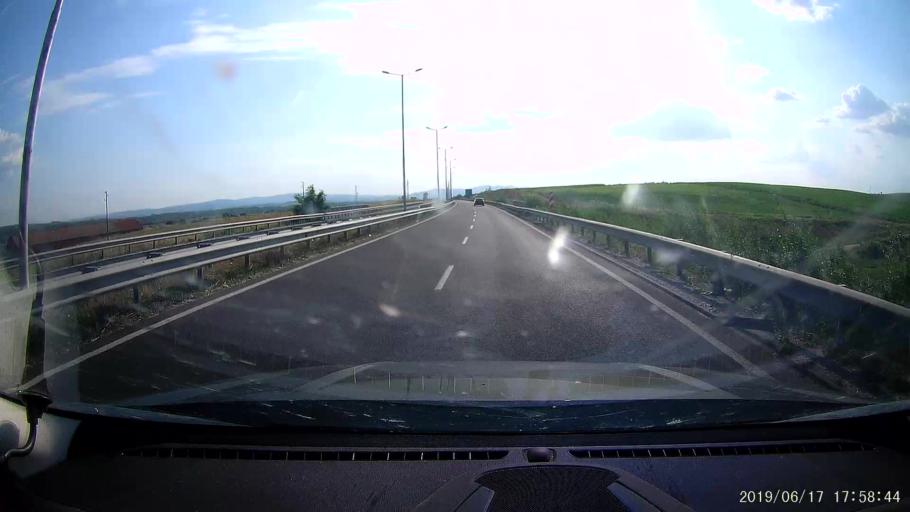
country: BG
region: Khaskovo
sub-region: Obshtina Svilengrad
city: Svilengrad
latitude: 41.7261
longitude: 26.3152
